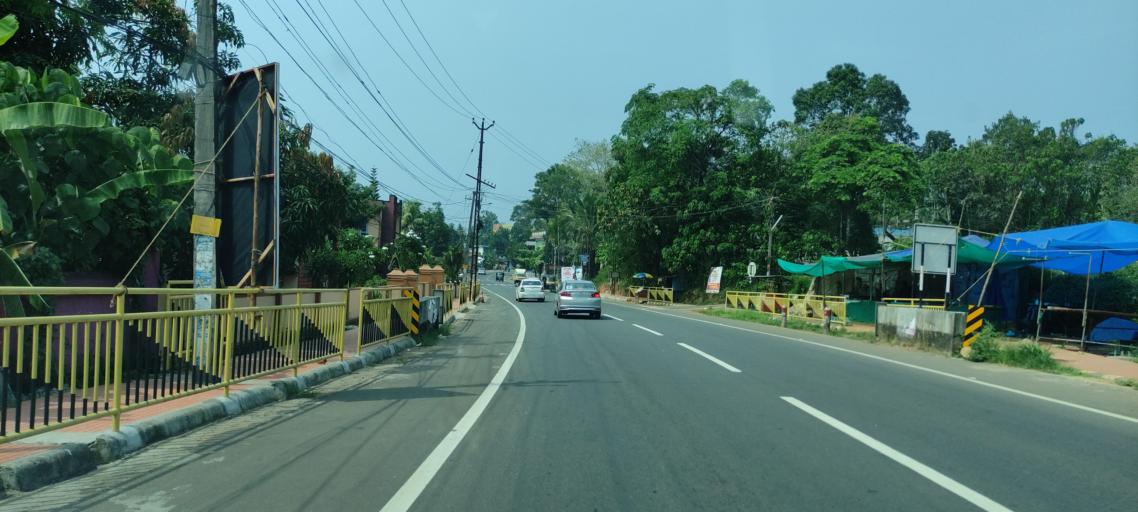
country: IN
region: Kerala
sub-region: Pattanamtitta
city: Adur
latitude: 9.1986
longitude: 76.6965
